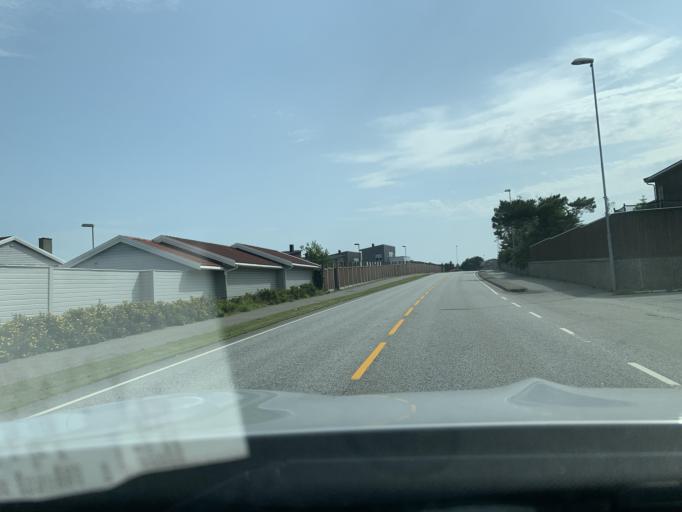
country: NO
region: Rogaland
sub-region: Klepp
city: Kleppe
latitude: 58.7697
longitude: 5.6297
